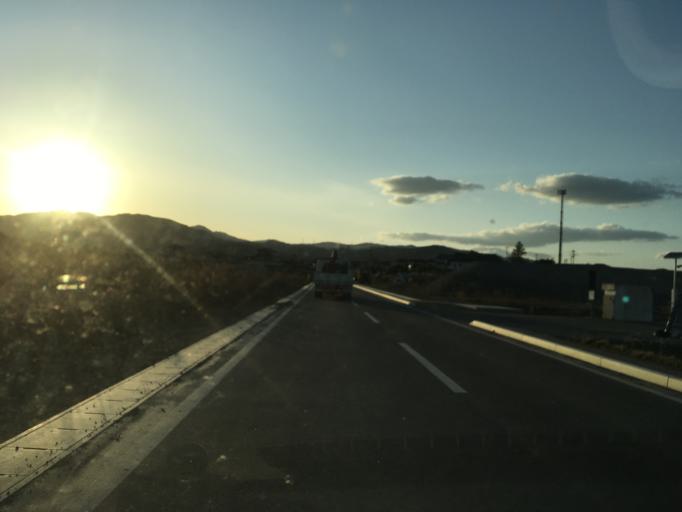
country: JP
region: Iwate
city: Ofunato
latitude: 38.8299
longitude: 141.5906
